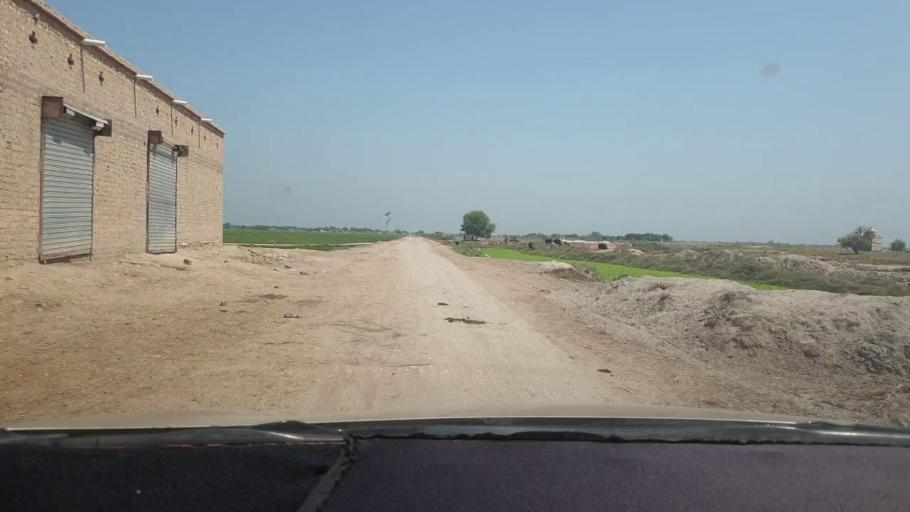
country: PK
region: Sindh
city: Miro Khan
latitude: 27.6896
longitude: 68.0798
